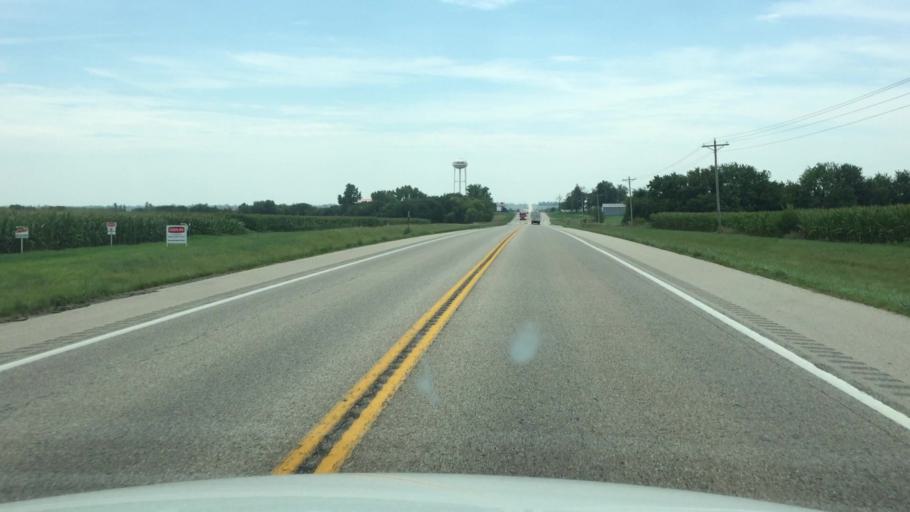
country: US
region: Kansas
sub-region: Nemaha County
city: Sabetha
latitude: 39.7090
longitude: -95.7301
